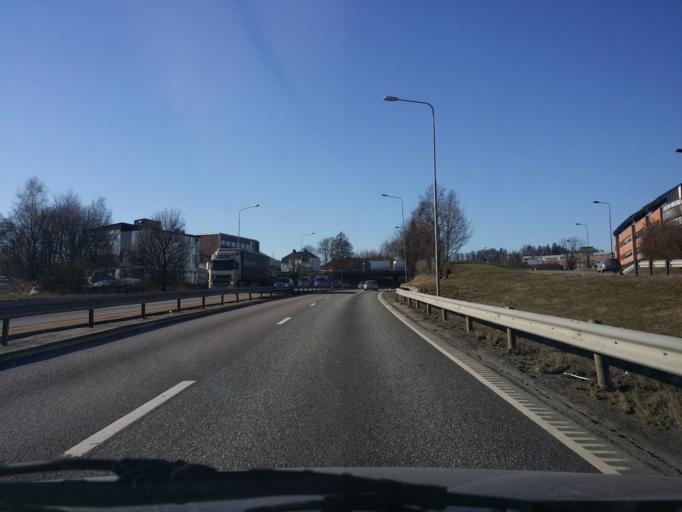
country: NO
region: Akershus
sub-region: Asker
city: Asker
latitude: 59.8343
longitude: 10.4421
